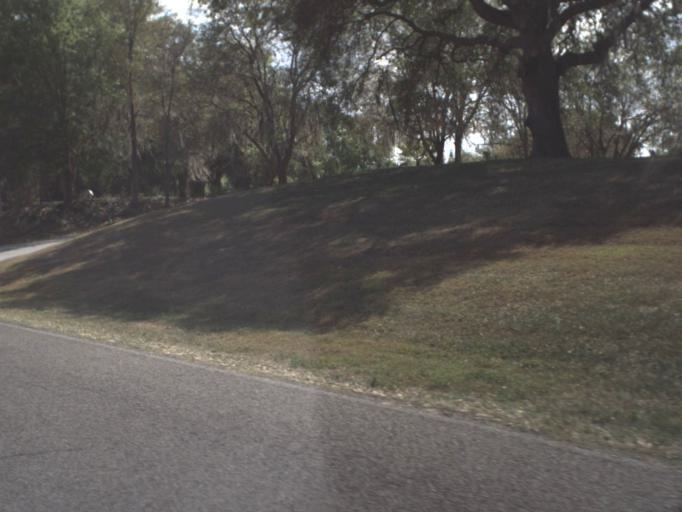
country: US
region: Florida
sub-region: Lake County
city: Hawthorne
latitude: 28.7583
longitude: -81.8793
